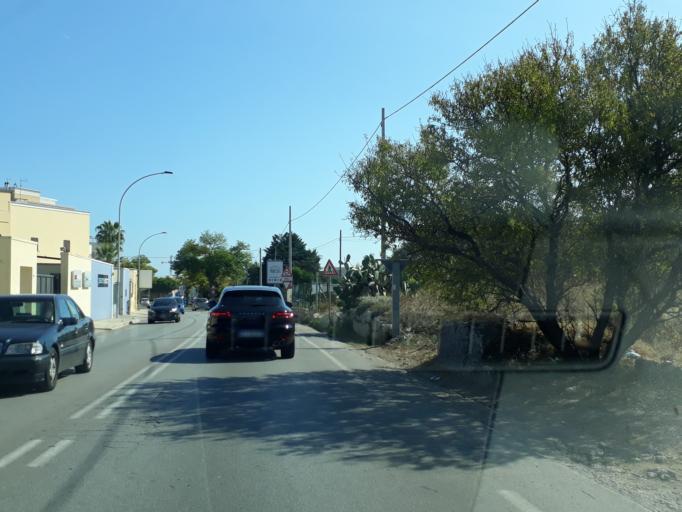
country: IT
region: Apulia
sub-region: Provincia di Bari
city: Monopoli
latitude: 40.9435
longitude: 17.3011
